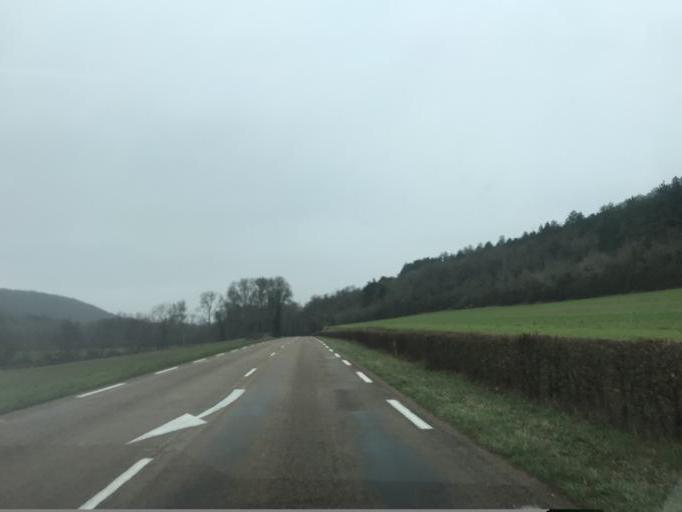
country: FR
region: Bourgogne
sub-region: Departement de l'Yonne
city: Avallon
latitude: 47.5226
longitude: 3.7764
